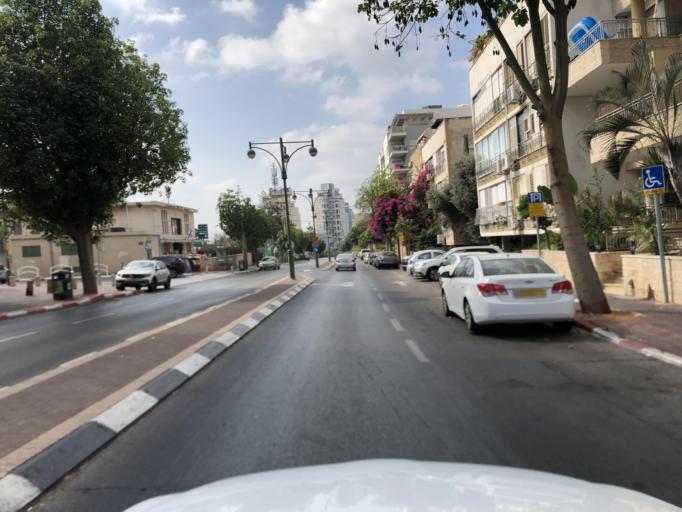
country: IL
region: Tel Aviv
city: Bene Beraq
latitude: 32.0691
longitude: 34.8326
